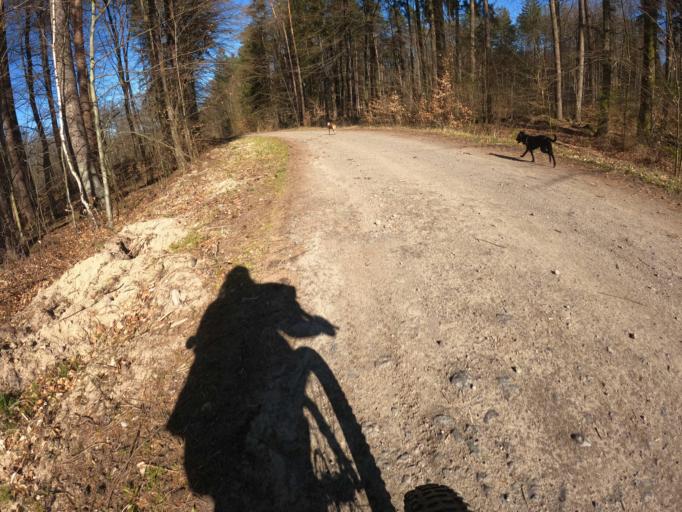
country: PL
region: West Pomeranian Voivodeship
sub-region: Powiat gryficki
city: Brojce
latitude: 54.0314
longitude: 15.4262
